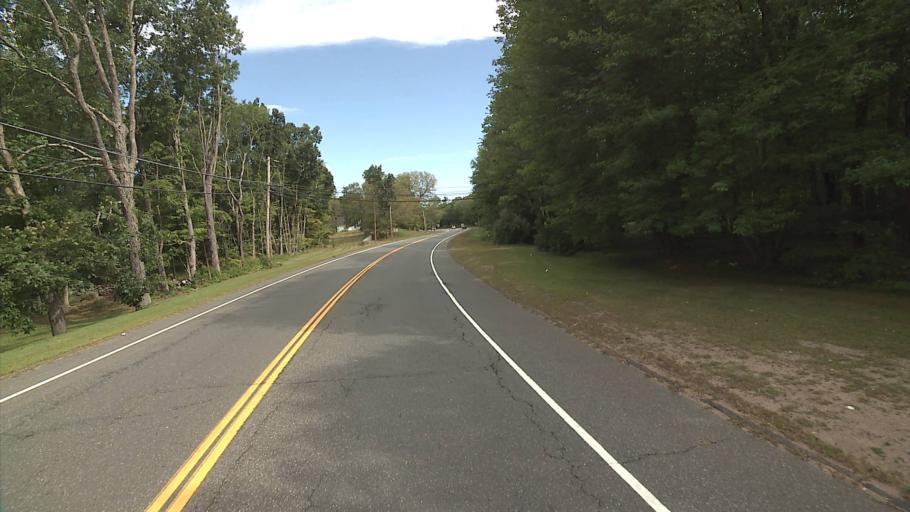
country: US
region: Connecticut
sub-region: Tolland County
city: Mansfield City
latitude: 41.7464
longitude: -72.2608
